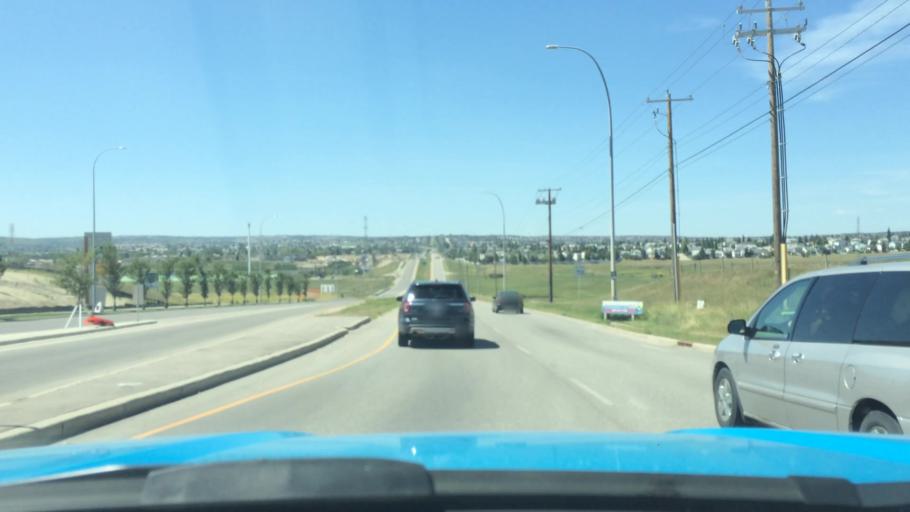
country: CA
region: Alberta
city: Calgary
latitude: 51.1544
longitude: -114.0283
